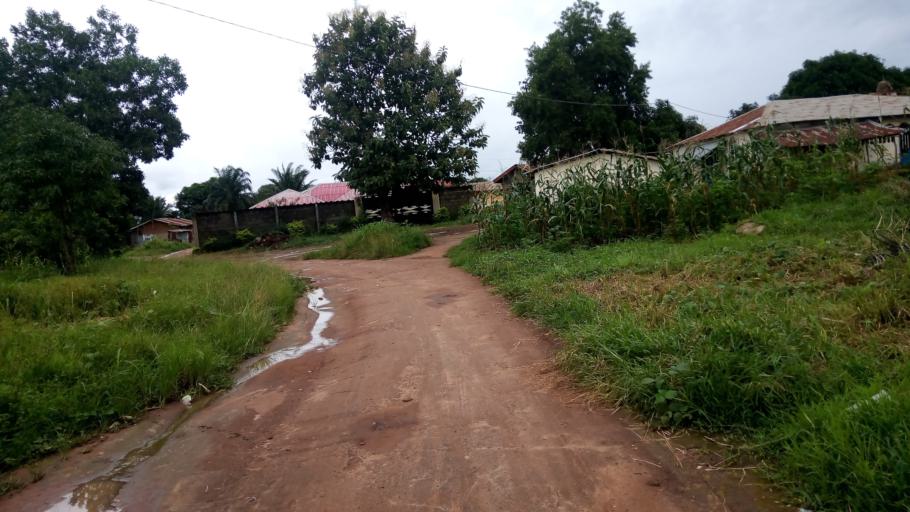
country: SL
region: Northern Province
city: Lunsar
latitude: 8.6923
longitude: -12.5312
